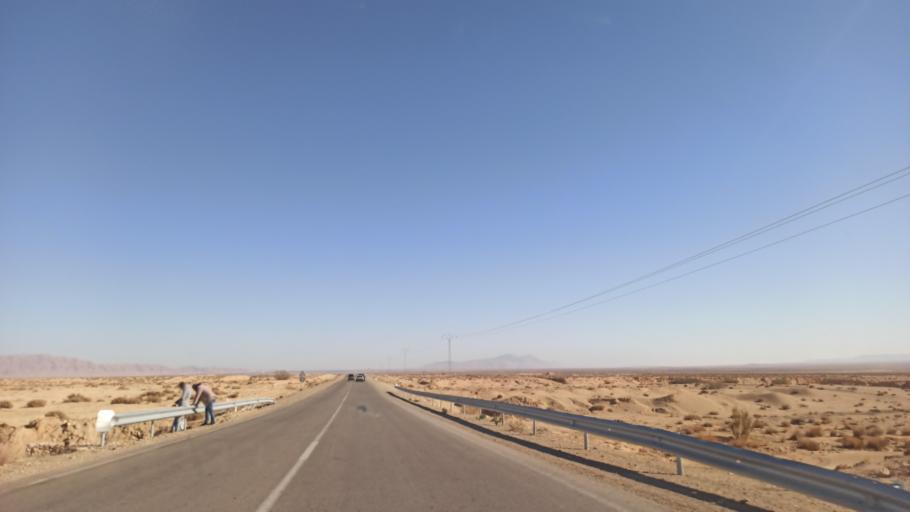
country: TN
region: Gafsa
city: Al Metlaoui
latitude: 34.3260
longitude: 8.5381
